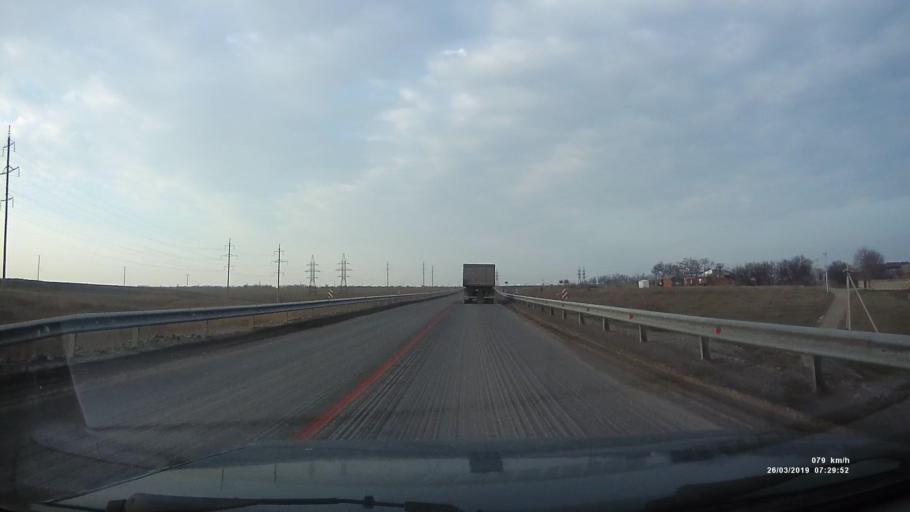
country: RU
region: Rostov
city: Novobessergenovka
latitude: 47.2412
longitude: 38.8130
